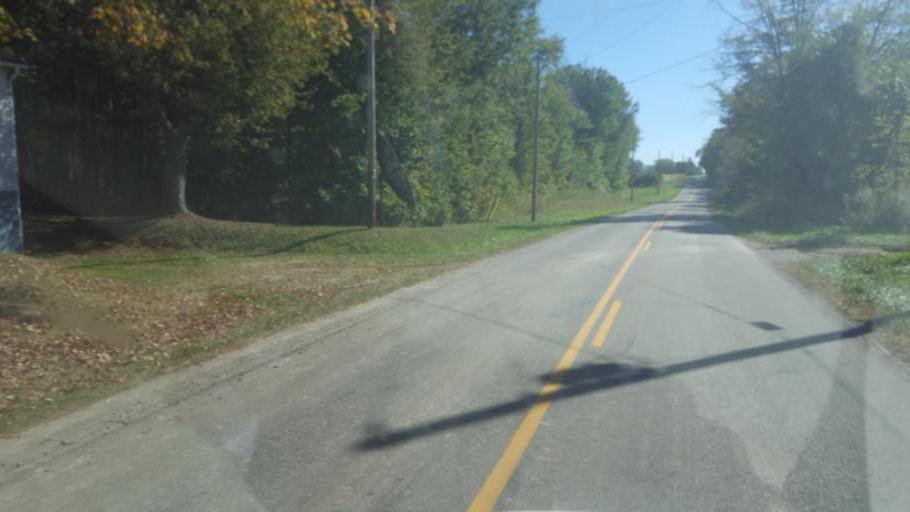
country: US
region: Ohio
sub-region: Wayne County
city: West Salem
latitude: 40.8864
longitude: -82.1740
